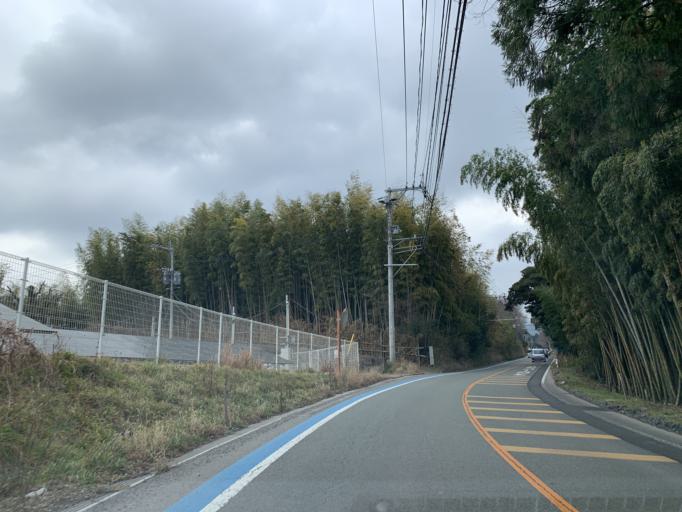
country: JP
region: Kumamoto
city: Ozu
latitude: 32.8949
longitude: 130.9240
